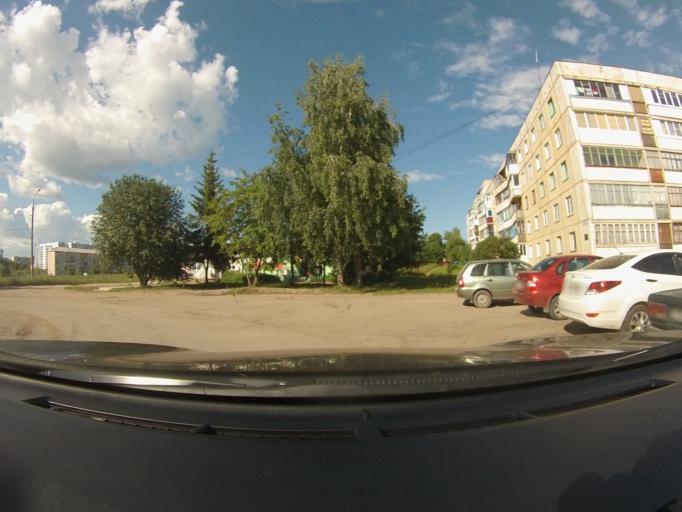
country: RU
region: Orjol
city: Mtsensk
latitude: 53.2867
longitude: 36.6043
